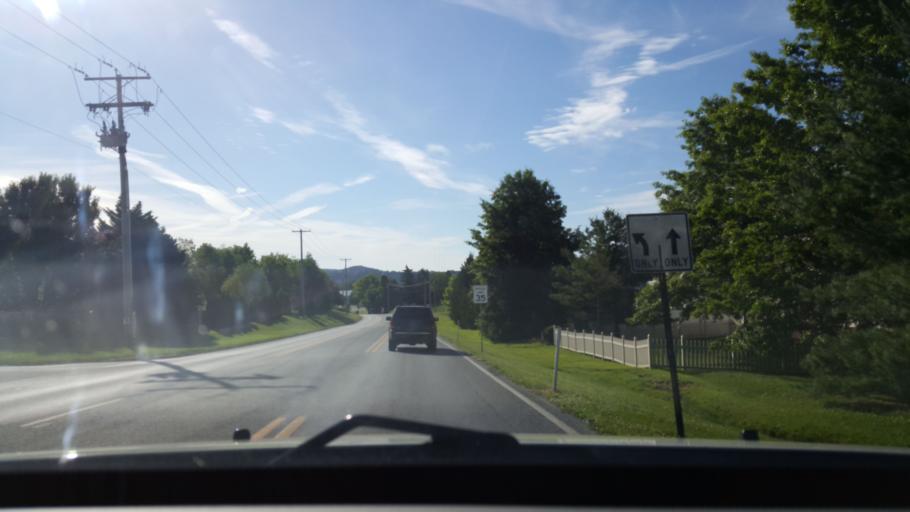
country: US
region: Pennsylvania
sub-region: York County
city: Emigsville
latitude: 40.0035
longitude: -76.7583
